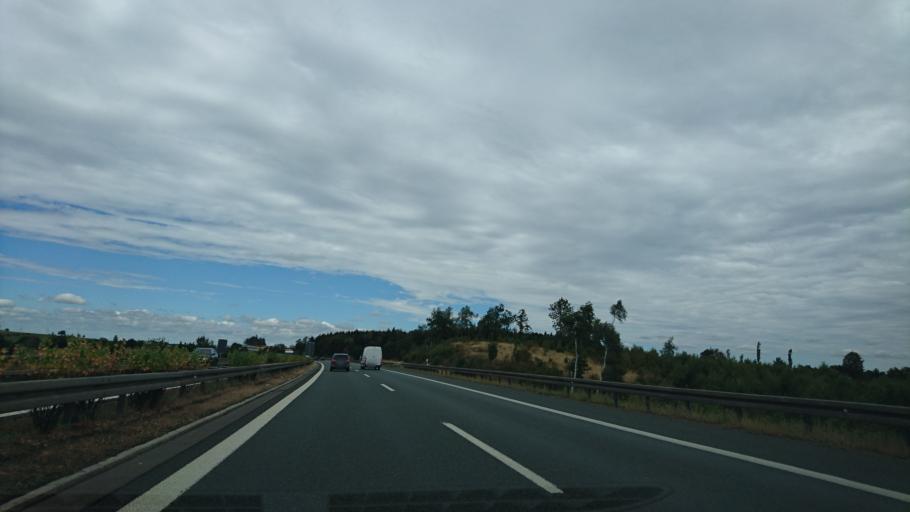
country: DE
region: Bavaria
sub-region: Upper Franconia
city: Gattendorf
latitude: 50.3383
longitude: 12.0122
